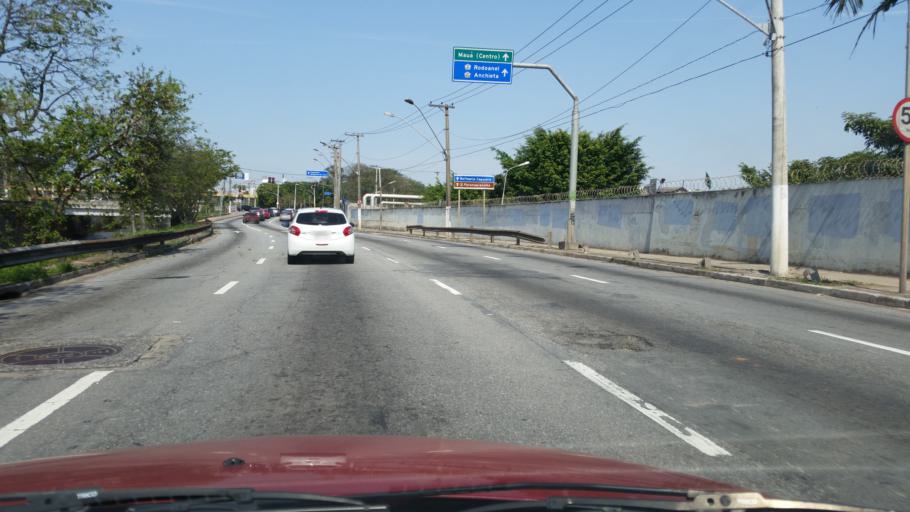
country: BR
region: Sao Paulo
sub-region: Santo Andre
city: Santo Andre
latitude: -23.6479
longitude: -46.5270
